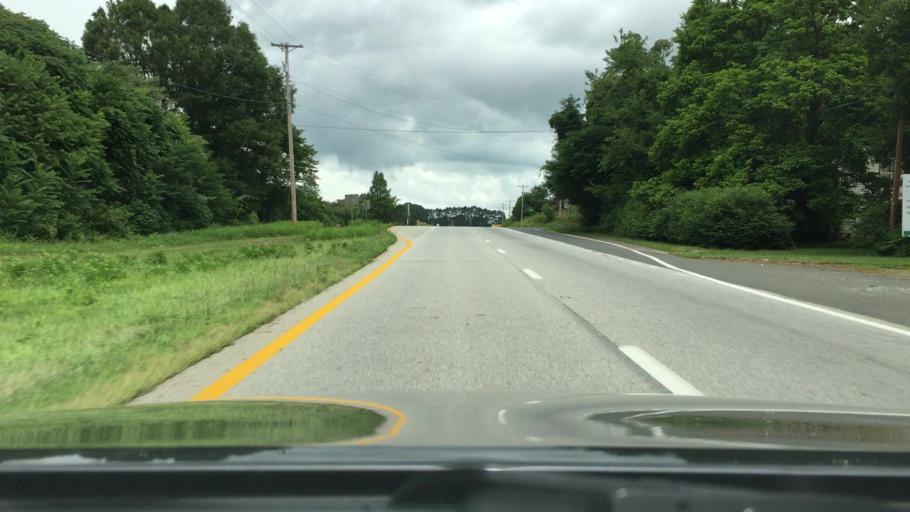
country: US
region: Virginia
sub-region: Amherst County
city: Amherst
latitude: 37.6127
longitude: -79.0175
